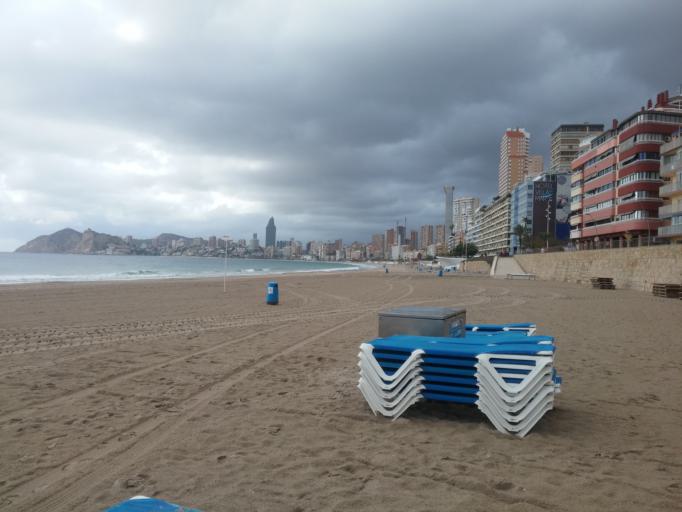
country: ES
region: Valencia
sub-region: Provincia de Alicante
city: Benidorm
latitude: 38.5370
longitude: -0.1360
